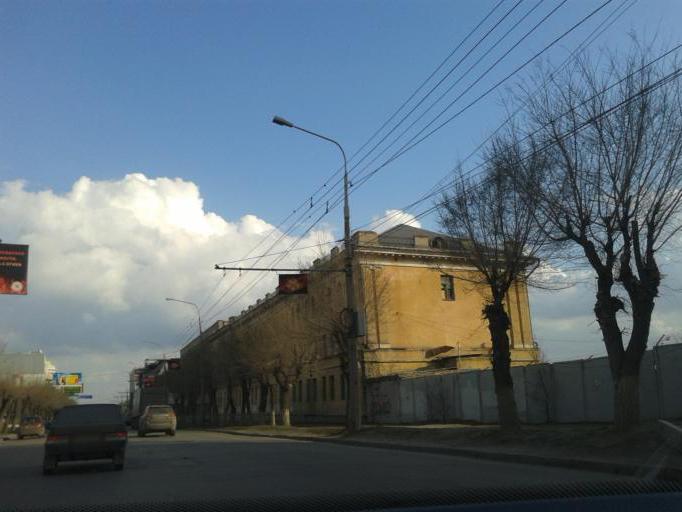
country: RU
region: Volgograd
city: Volgograd
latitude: 48.7208
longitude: 44.5041
